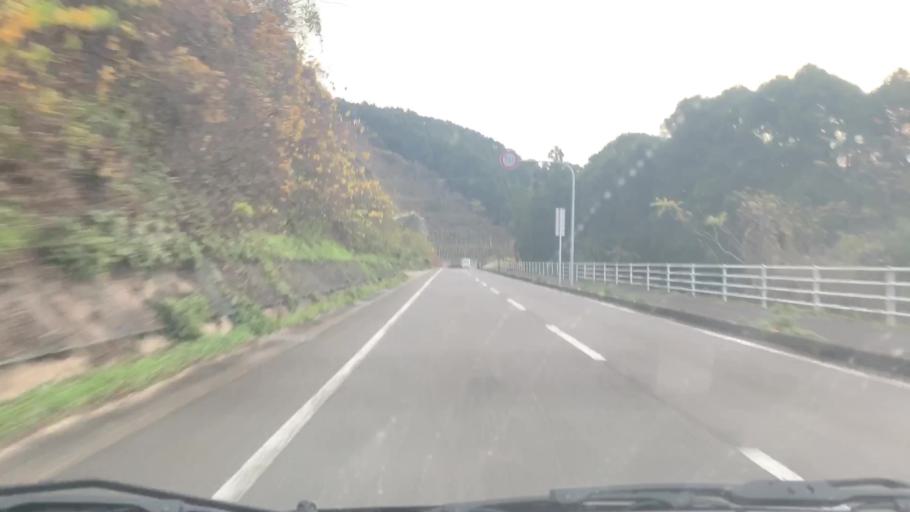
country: JP
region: Saga Prefecture
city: Kashima
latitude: 33.0434
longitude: 130.0717
